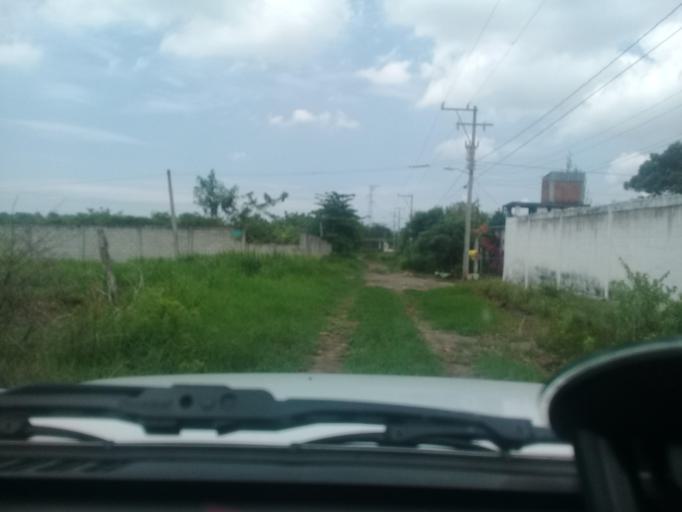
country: MX
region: Veracruz
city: Paso de Ovejas
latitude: 19.2932
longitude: -96.4404
